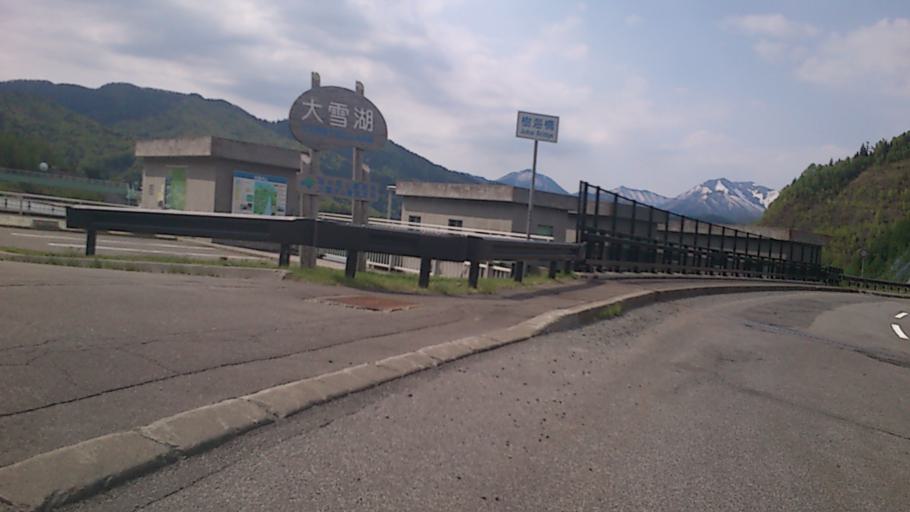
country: JP
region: Hokkaido
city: Kamikawa
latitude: 43.6782
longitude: 143.0375
